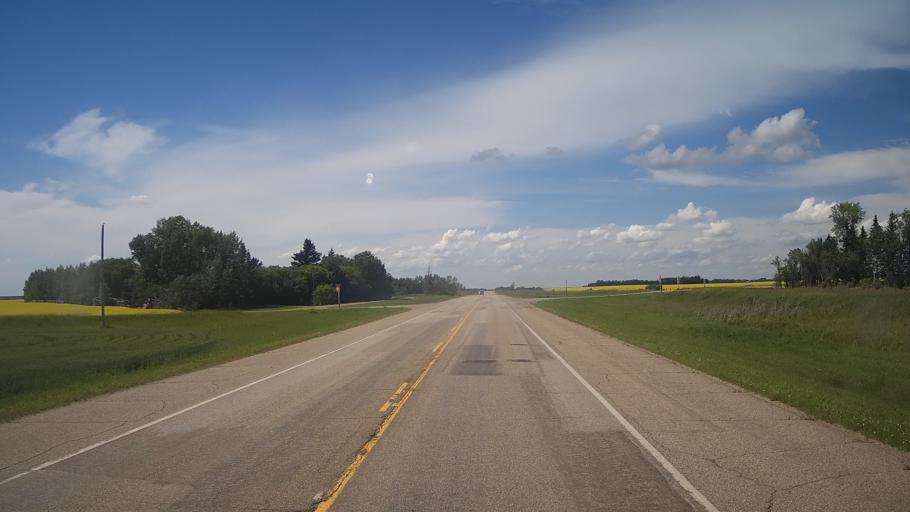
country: CA
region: Saskatchewan
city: Yorkton
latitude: 51.0907
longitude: -102.2621
